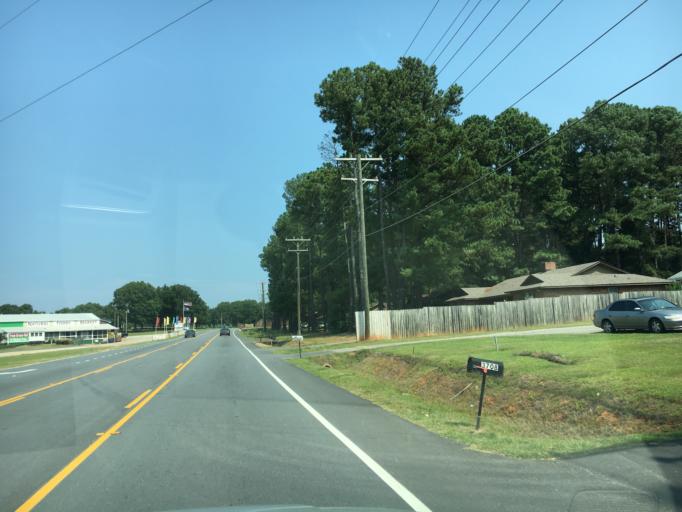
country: US
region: South Carolina
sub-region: Spartanburg County
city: Valley Falls
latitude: 35.0262
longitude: -81.9500
